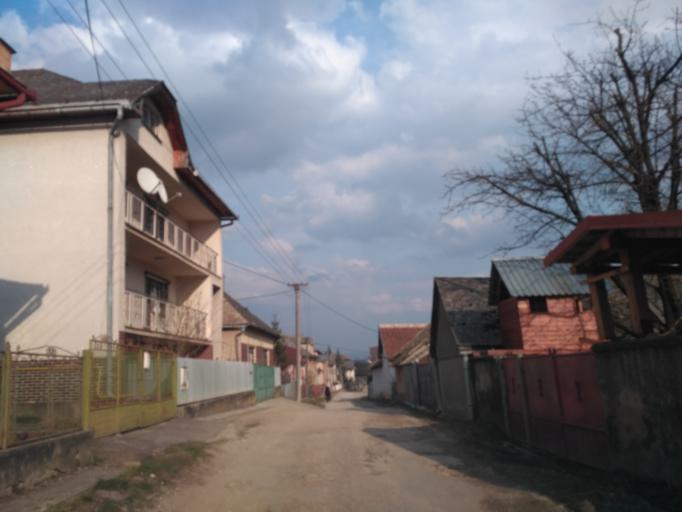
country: SK
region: Kosicky
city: Roznava
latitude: 48.6381
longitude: 20.4698
